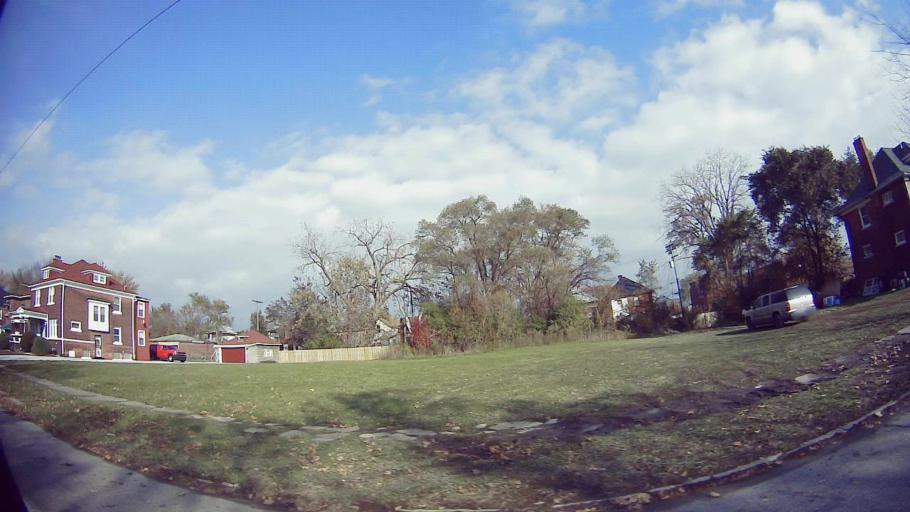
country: US
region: Michigan
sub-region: Wayne County
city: Detroit
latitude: 42.3425
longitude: -83.1059
